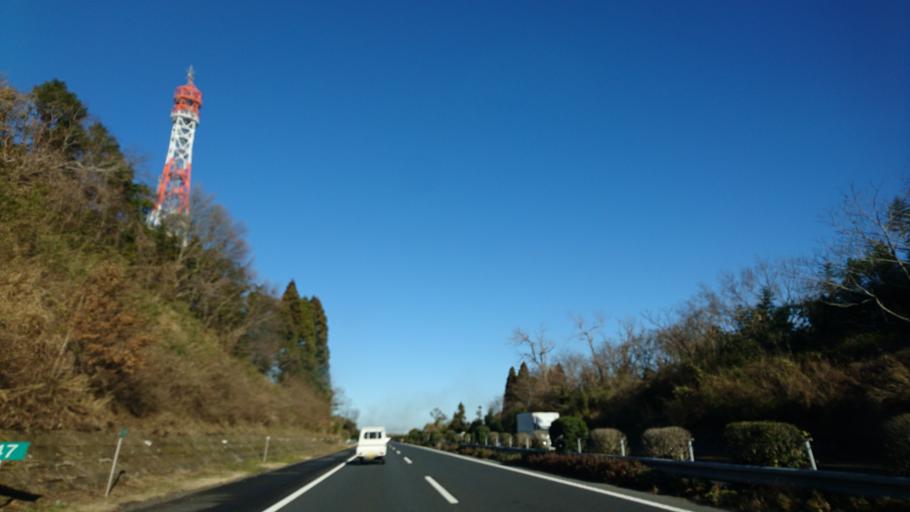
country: JP
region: Chiba
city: Ichihara
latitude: 35.4700
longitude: 140.0842
